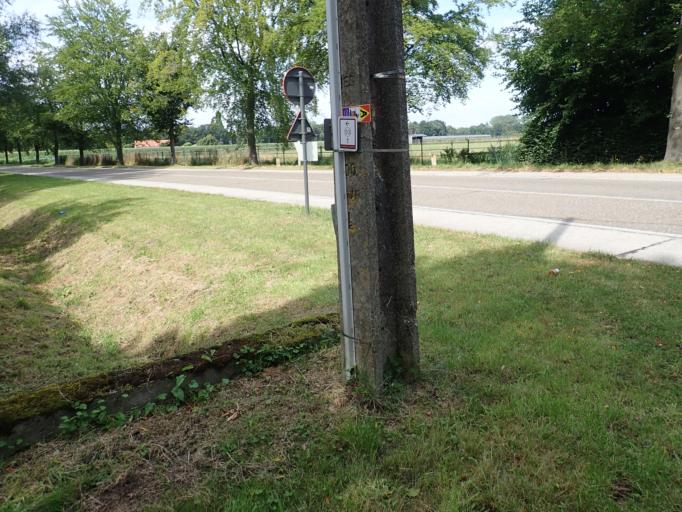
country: BE
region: Flanders
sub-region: Provincie Antwerpen
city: Zandhoven
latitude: 51.1993
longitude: 4.6652
